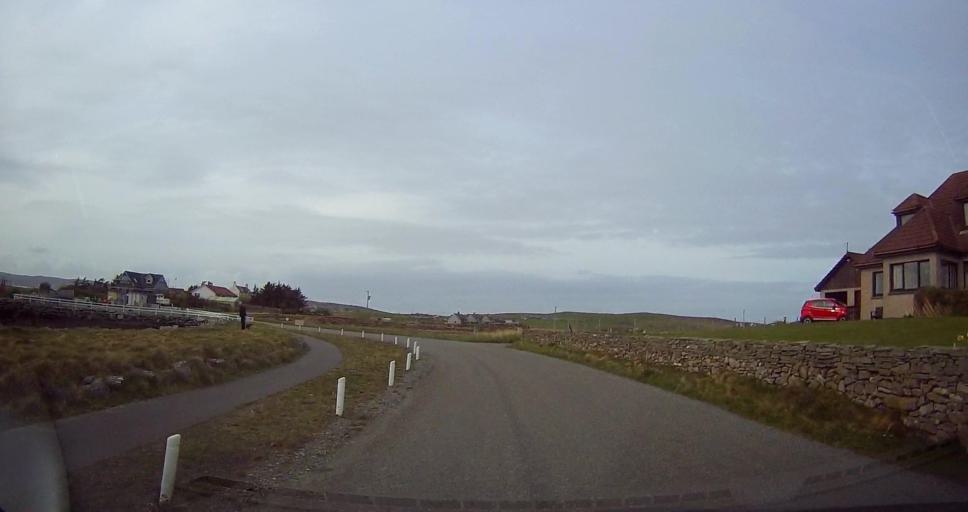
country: GB
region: Scotland
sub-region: Shetland Islands
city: Shetland
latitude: 60.1507
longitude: -1.1138
